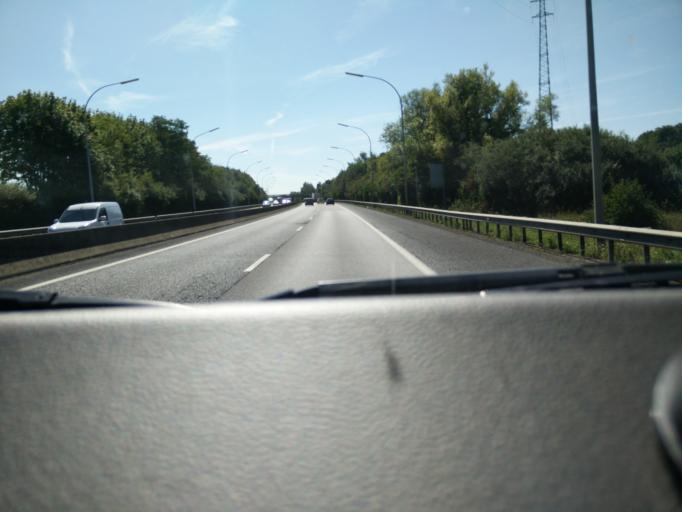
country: LU
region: Luxembourg
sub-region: Canton de Luxembourg
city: Strassen
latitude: 49.5985
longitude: 6.0799
